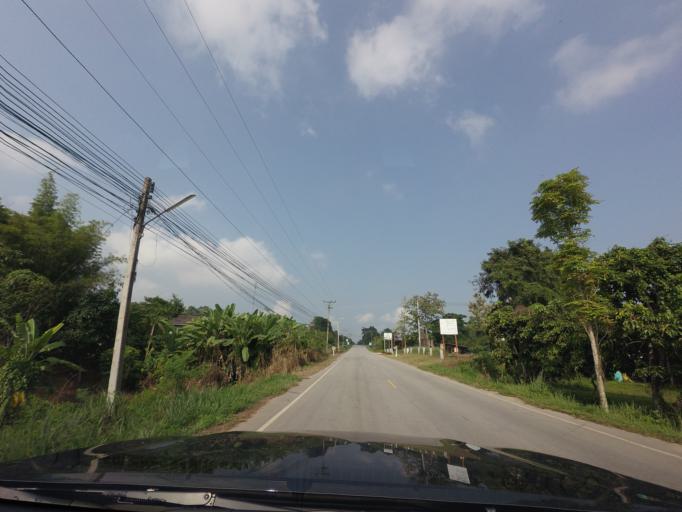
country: TH
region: Loei
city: Chiang Khan
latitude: 17.8903
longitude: 101.6381
